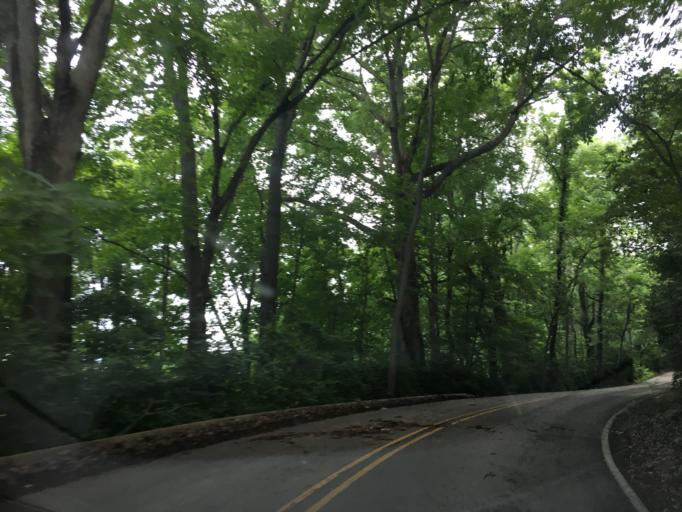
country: US
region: Tennessee
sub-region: Davidson County
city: Forest Hills
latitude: 36.0814
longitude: -86.8289
